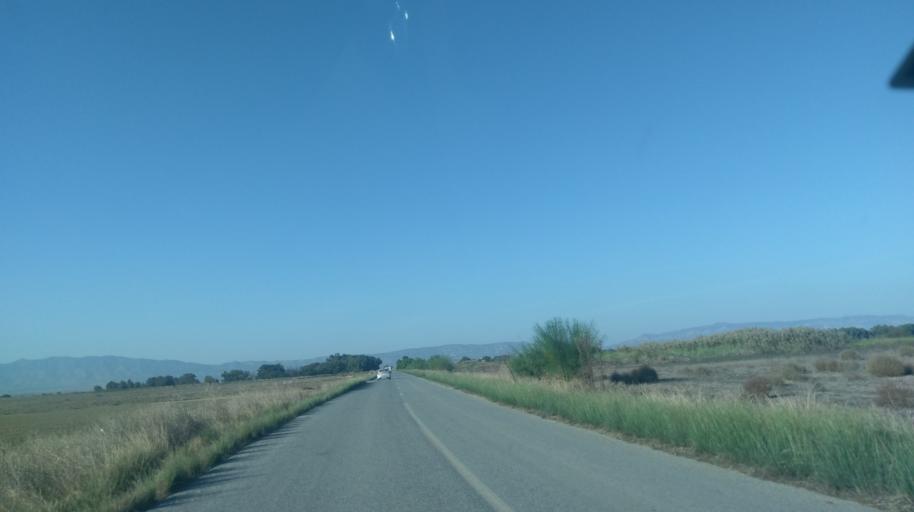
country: CY
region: Ammochostos
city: Lefkonoiko
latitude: 35.1955
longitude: 33.6960
